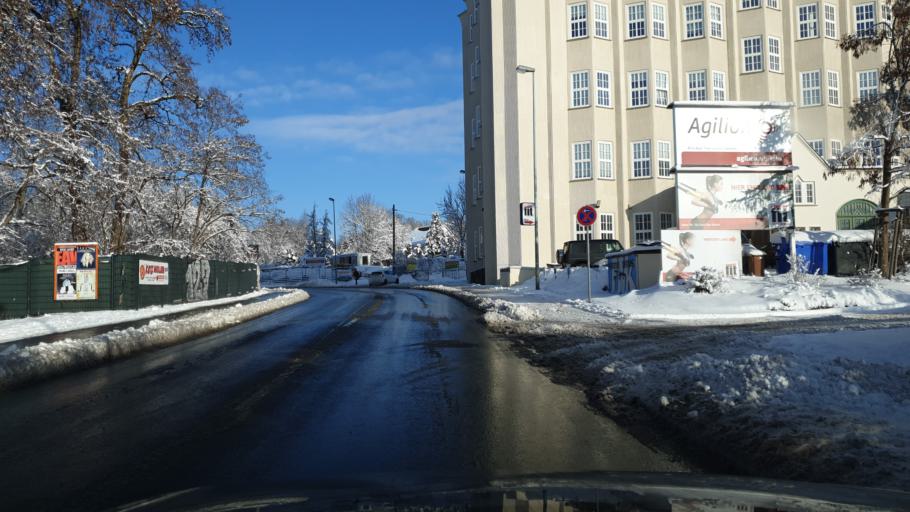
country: DE
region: Saxony
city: Chemnitz
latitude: 50.8572
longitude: 12.9294
